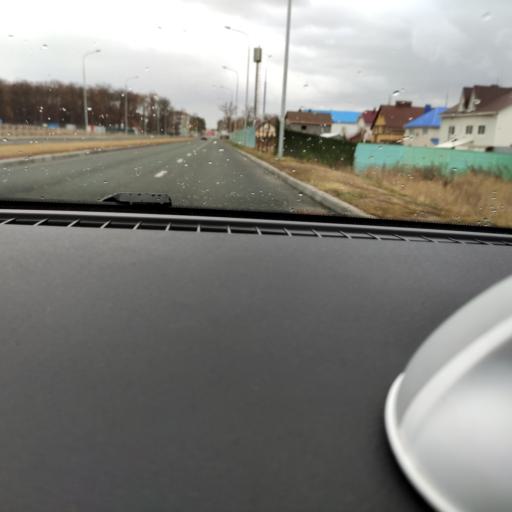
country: RU
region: Samara
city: Samara
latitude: 53.2700
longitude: 50.2352
